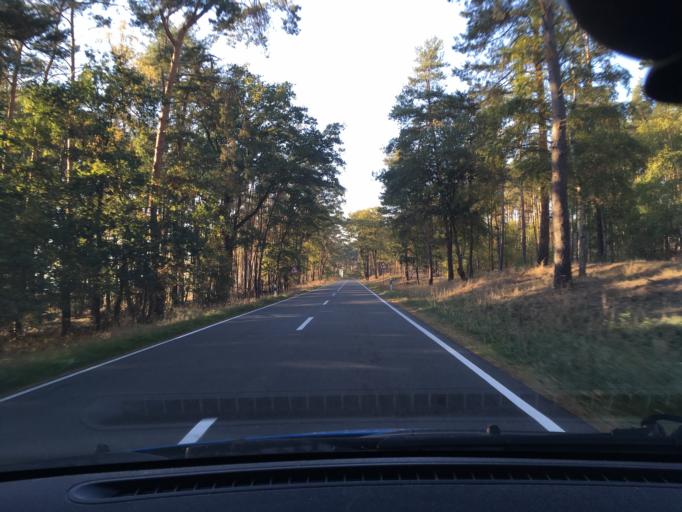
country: DE
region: Lower Saxony
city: Neu Darchau
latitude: 53.2715
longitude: 10.9451
